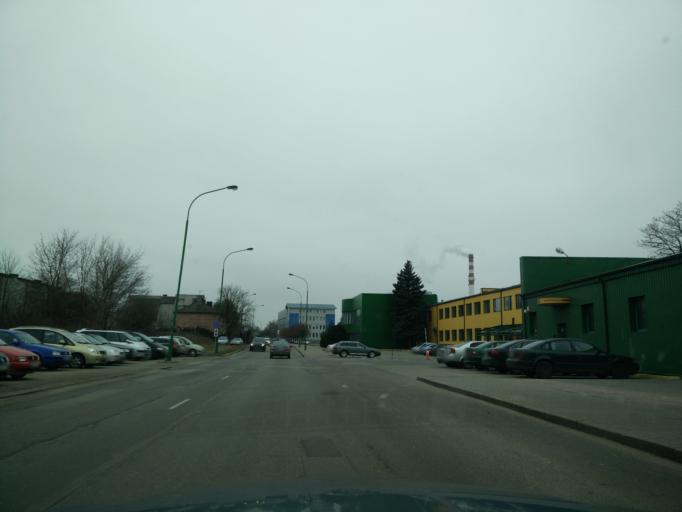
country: LT
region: Klaipedos apskritis
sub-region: Klaipeda
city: Klaipeda
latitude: 55.7140
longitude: 21.1556
